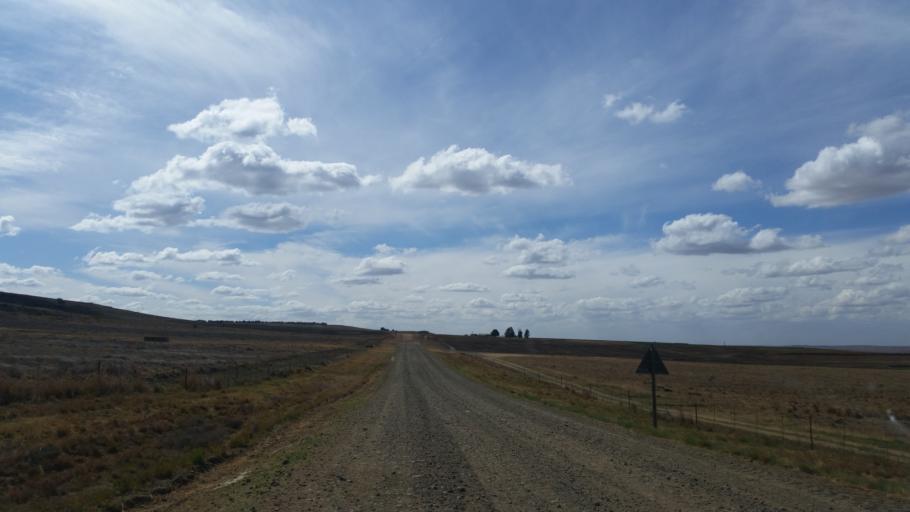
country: ZA
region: Orange Free State
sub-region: Thabo Mofutsanyana District Municipality
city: Bethlehem
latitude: -28.1797
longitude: 28.5049
